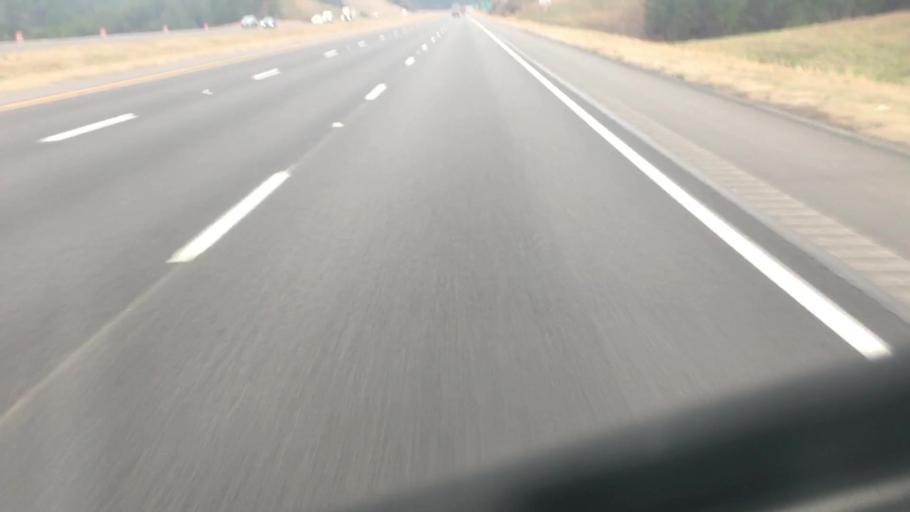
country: US
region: Alabama
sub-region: Walker County
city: Cordova
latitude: 33.7267
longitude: -87.1902
